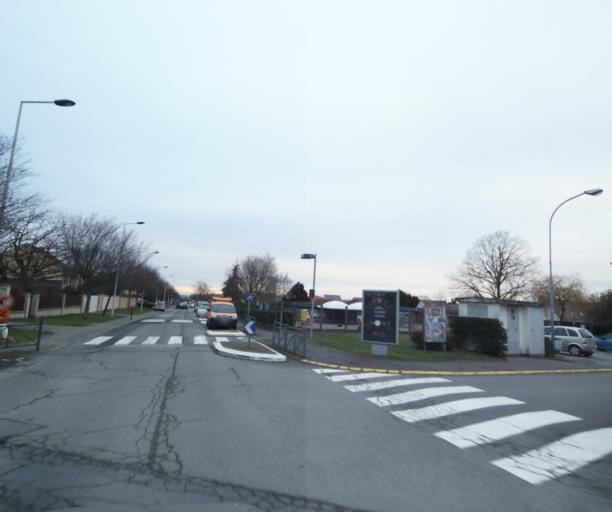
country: FR
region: Ile-de-France
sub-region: Departement de Seine-et-Marne
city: Dammartin-en-Goele
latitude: 49.0623
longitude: 2.6869
